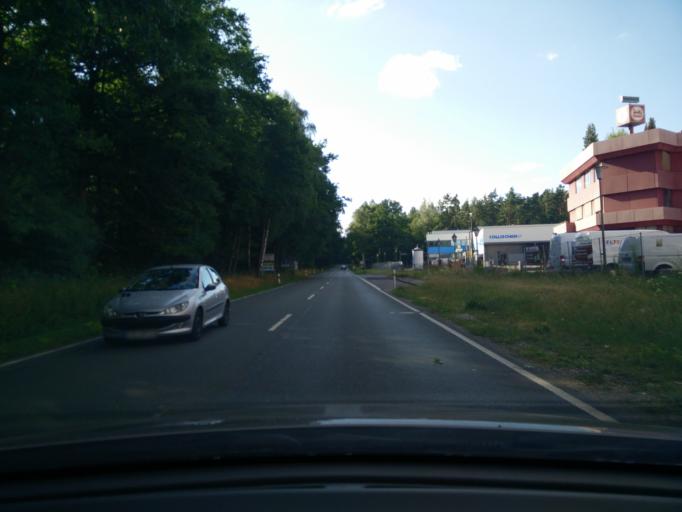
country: DE
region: Bavaria
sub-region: Regierungsbezirk Mittelfranken
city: Wendelstein
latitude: 49.4130
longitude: 11.1582
